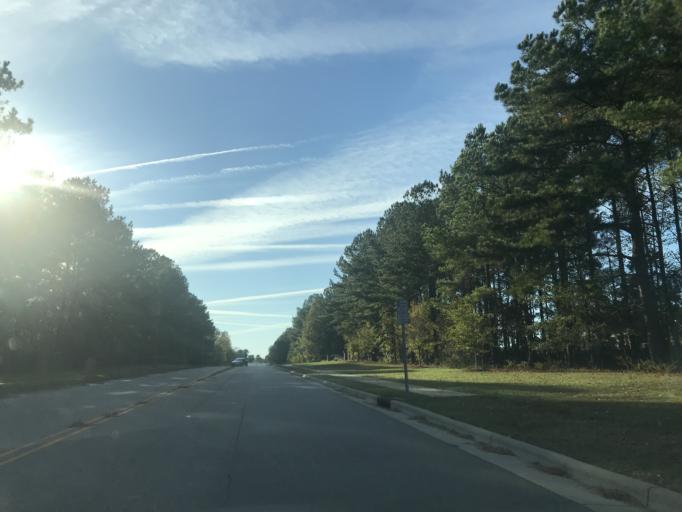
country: US
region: North Carolina
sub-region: Wake County
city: Wake Forest
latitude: 35.8916
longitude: -78.5524
